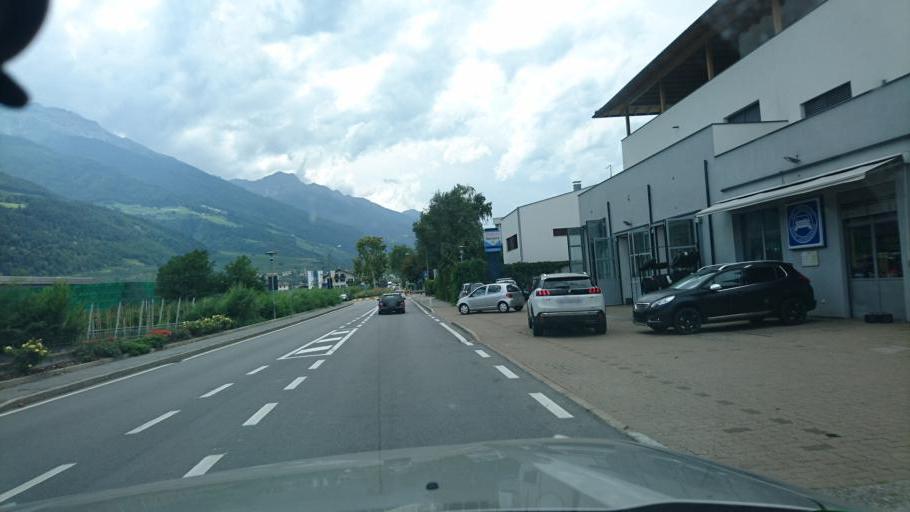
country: IT
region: Trentino-Alto Adige
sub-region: Bolzano
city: Silandro
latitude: 46.6259
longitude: 10.7797
